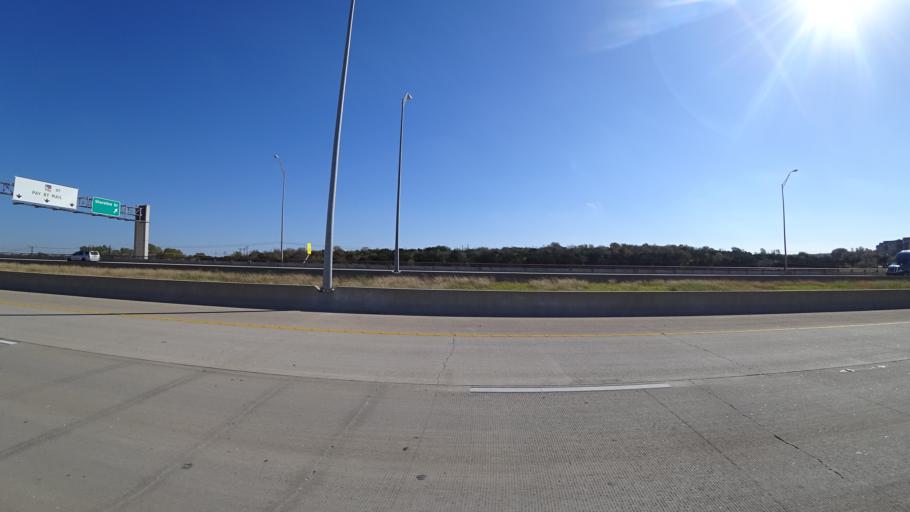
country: US
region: Texas
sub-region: Travis County
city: Wells Branch
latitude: 30.4477
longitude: -97.6964
